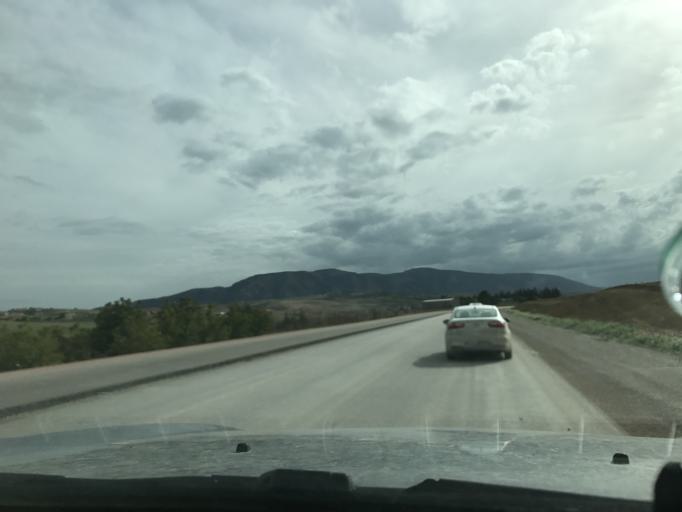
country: TN
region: Silyanah
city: Bu `Aradah
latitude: 36.1469
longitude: 9.6310
